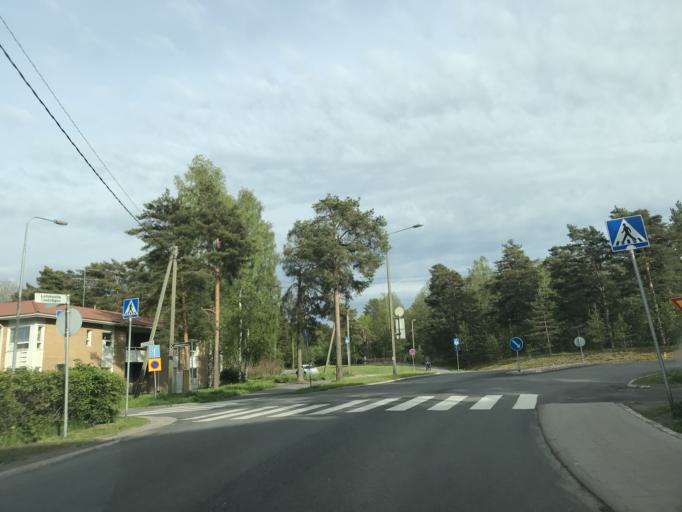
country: FI
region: Varsinais-Suomi
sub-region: Turku
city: Turku
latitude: 60.4372
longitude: 22.3088
